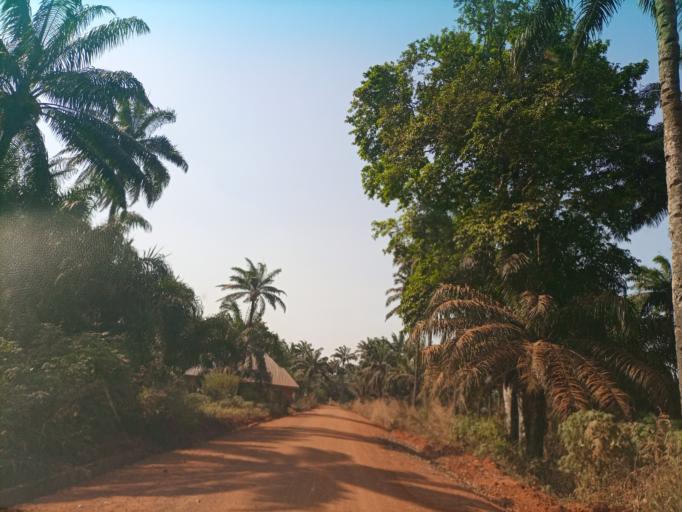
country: NG
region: Enugu
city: Aku
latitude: 6.7013
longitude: 7.3184
